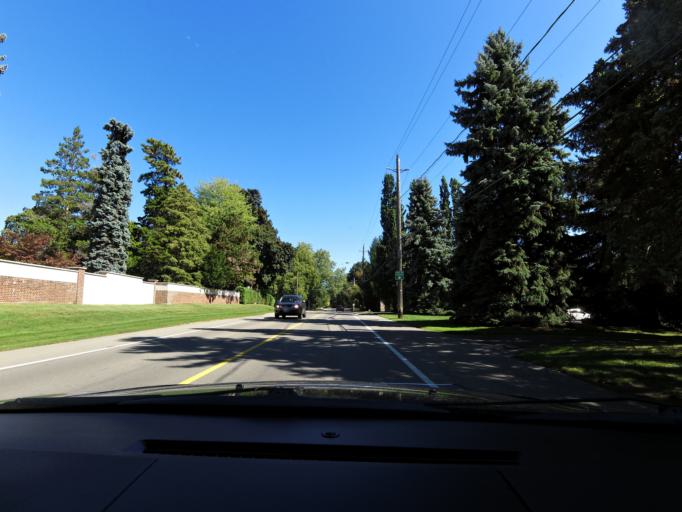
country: CA
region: Ontario
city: Hamilton
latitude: 43.3115
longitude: -79.8218
